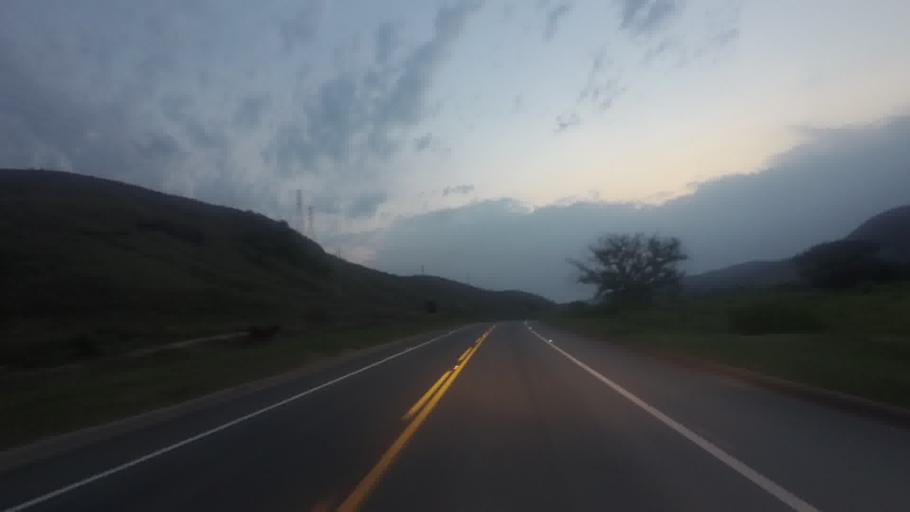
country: BR
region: Minas Gerais
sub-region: Alem Paraiba
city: Alem Paraiba
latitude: -21.9130
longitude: -42.7472
